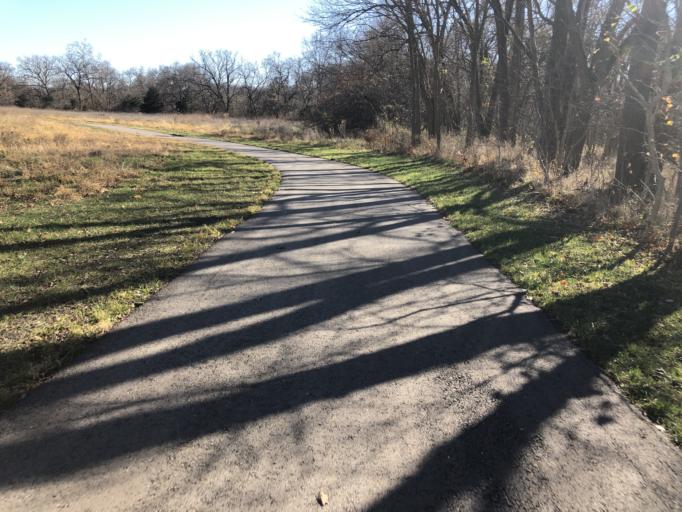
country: US
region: Kansas
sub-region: Johnson County
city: Gardner
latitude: 38.8737
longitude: -94.9545
